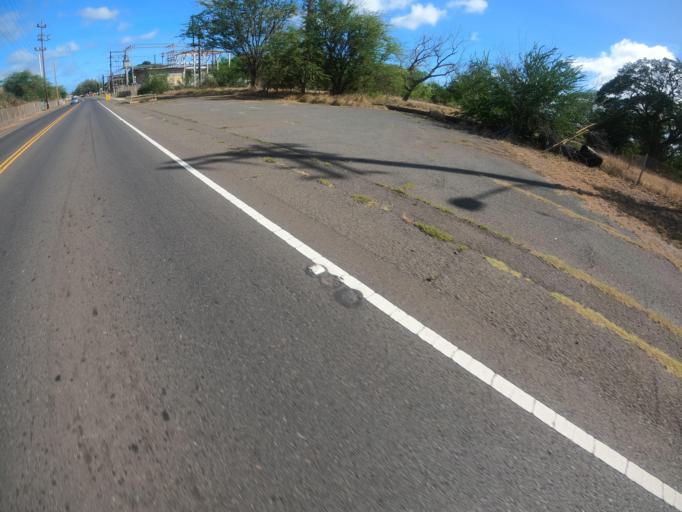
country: US
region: Hawaii
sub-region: Honolulu County
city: Makakilo City
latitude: 21.3233
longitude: -158.0794
